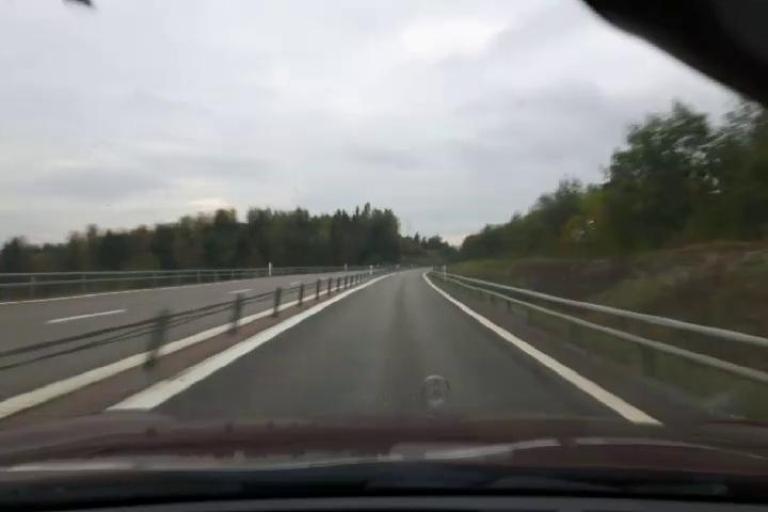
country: SE
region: Vaesternorrland
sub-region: Haernoesands Kommun
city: Haernoesand
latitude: 62.7109
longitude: 17.8898
